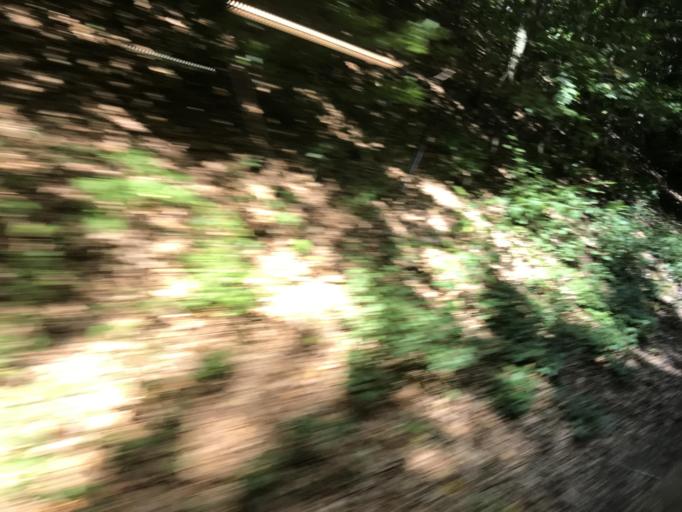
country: DE
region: Bavaria
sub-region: Regierungsbezirk Unterfranken
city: Schonau
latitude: 50.0729
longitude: 9.7189
